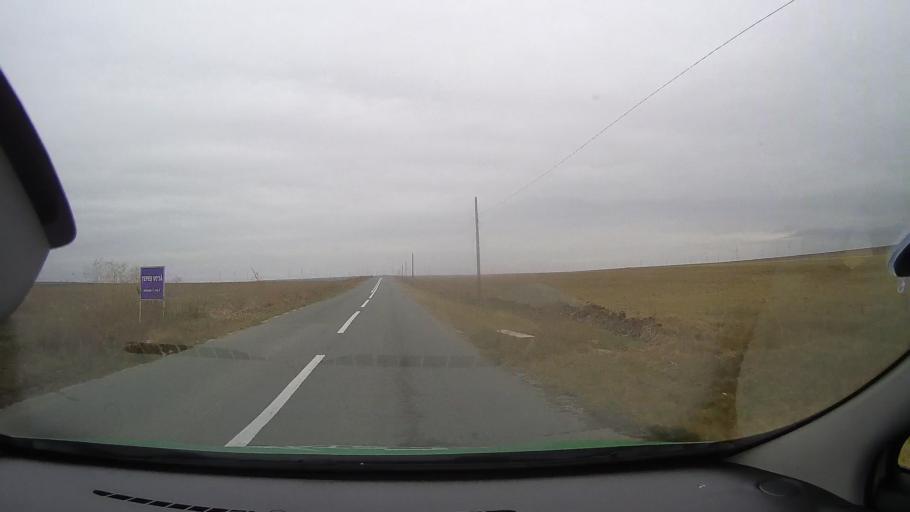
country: RO
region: Constanta
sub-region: Comuna Crucea
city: Crucea
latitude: 44.4522
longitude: 28.2484
